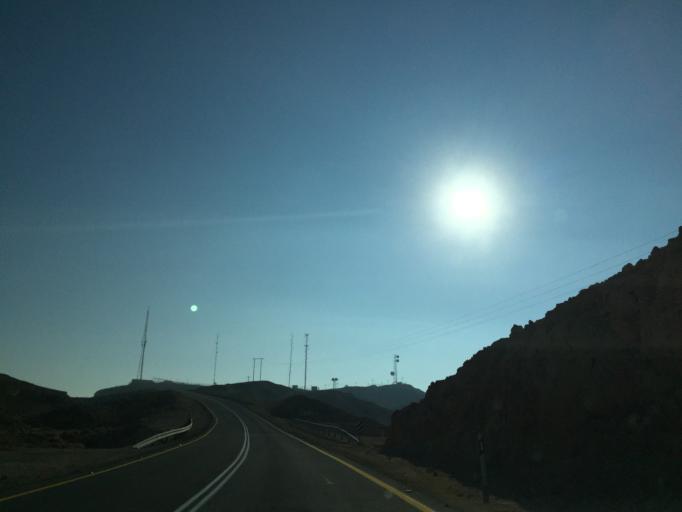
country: JO
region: Ma'an
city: Al Quwayrah
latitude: 30.0222
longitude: 35.0535
